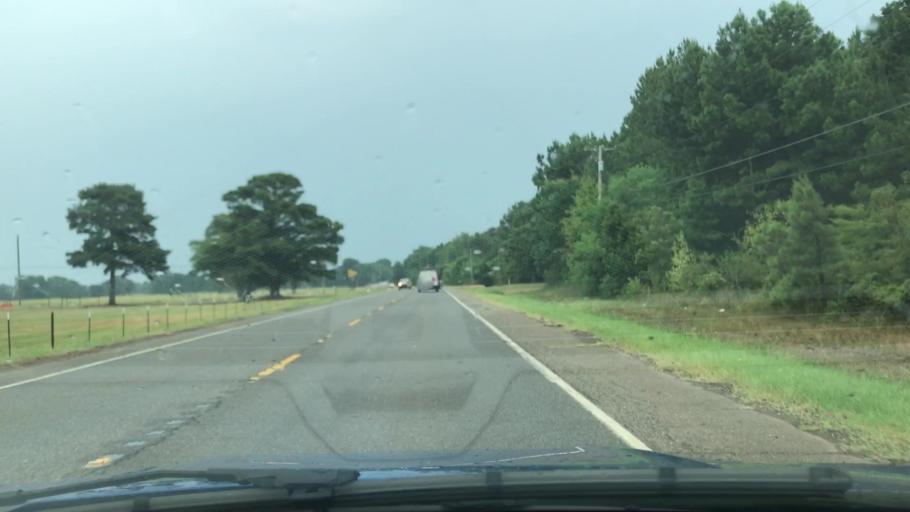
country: US
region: Texas
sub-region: Harrison County
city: Waskom
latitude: 32.4638
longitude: -94.0322
